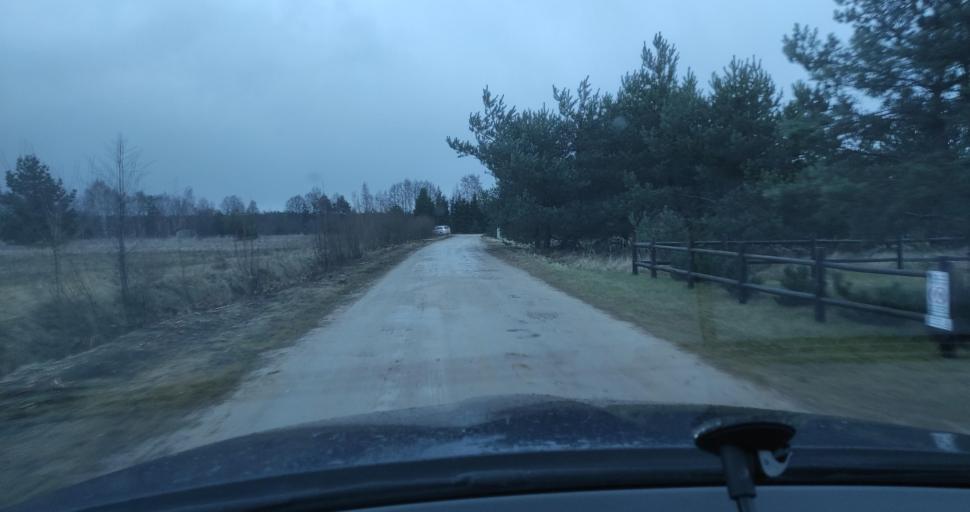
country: LV
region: Pavilostas
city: Pavilosta
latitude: 56.7439
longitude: 21.0683
